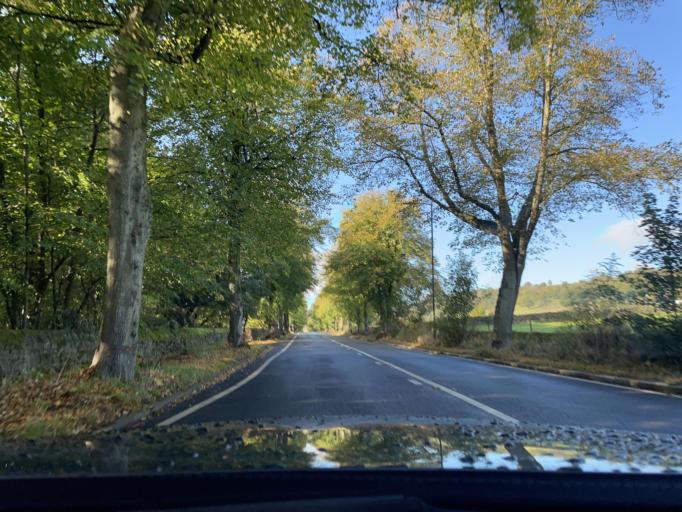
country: GB
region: England
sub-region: Sheffield
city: Bradfield
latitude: 53.3828
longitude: -1.5587
